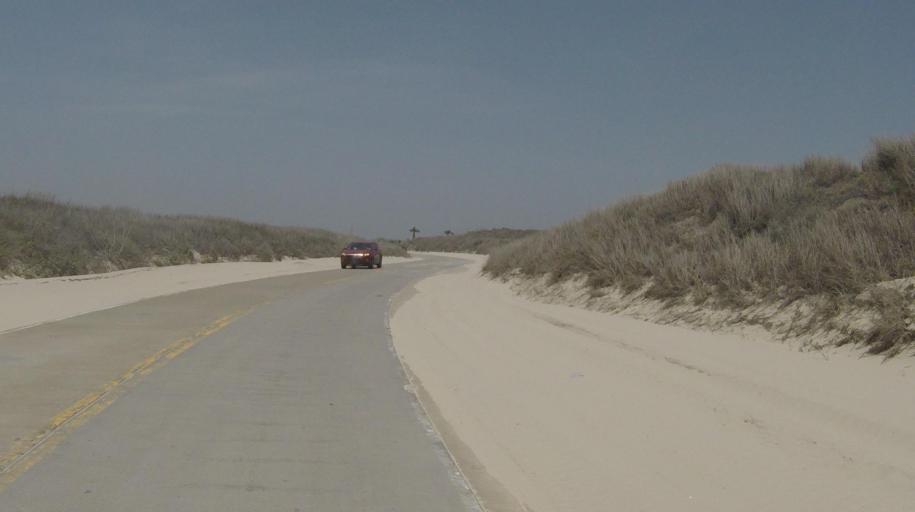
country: US
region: Texas
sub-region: Nueces County
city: Port Aransas
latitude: 27.6171
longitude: -97.2031
